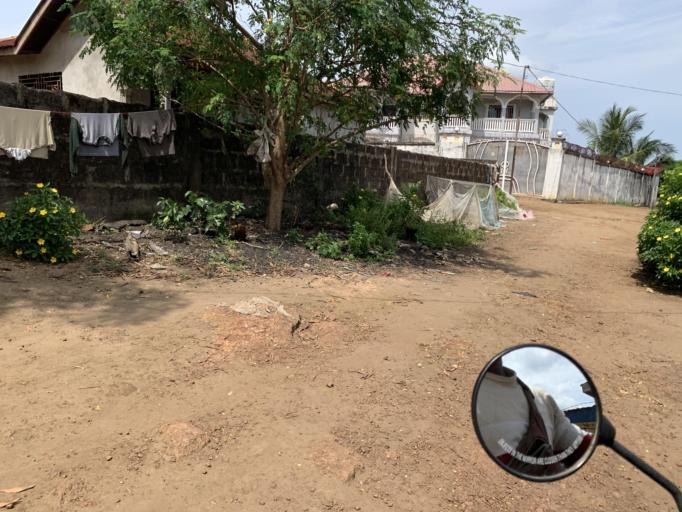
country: SL
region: Western Area
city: Hastings
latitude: 8.4043
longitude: -13.1341
